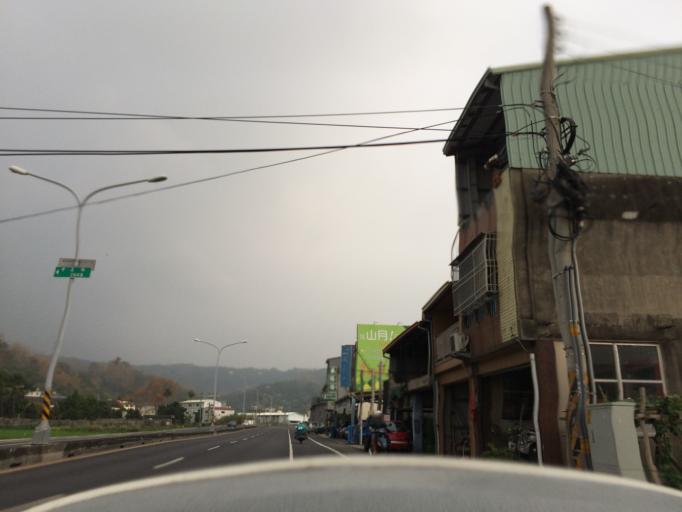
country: TW
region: Taiwan
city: Zhongxing New Village
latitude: 24.0331
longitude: 120.6945
